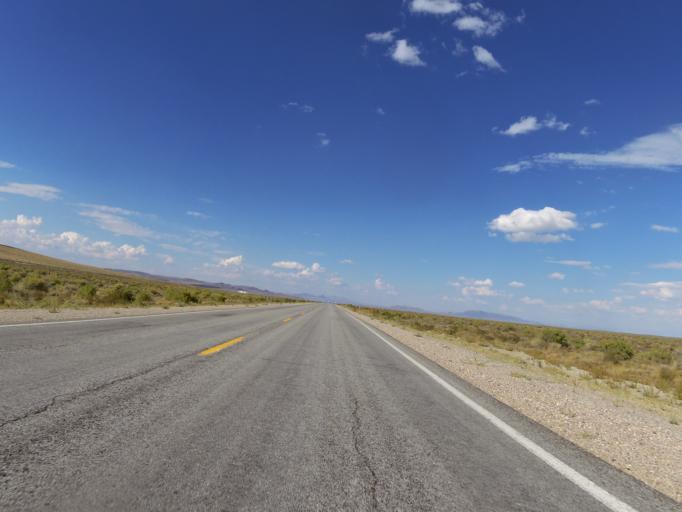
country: US
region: Nevada
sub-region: Churchill County
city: Fallon
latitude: 39.6384
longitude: -118.7828
